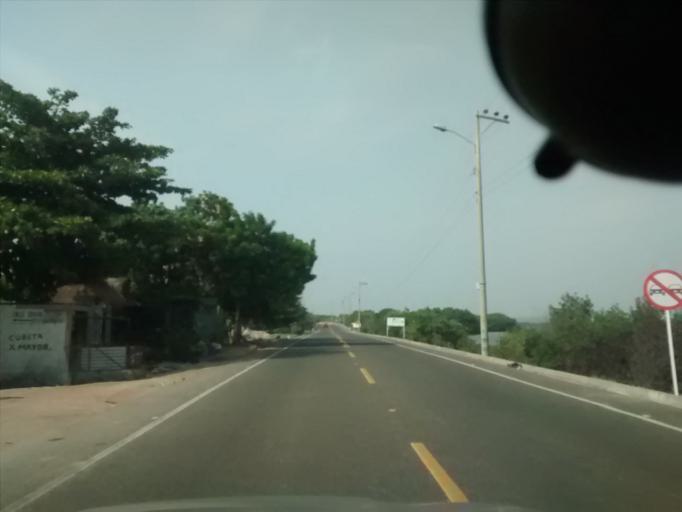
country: CO
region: Bolivar
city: Cartagena
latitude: 10.4764
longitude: -75.4919
